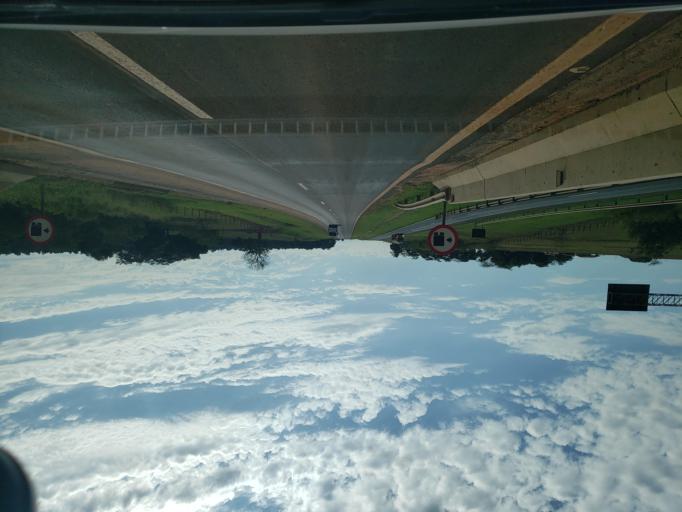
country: BR
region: Sao Paulo
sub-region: Promissao
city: Promissao
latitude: -21.6096
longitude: -49.8707
